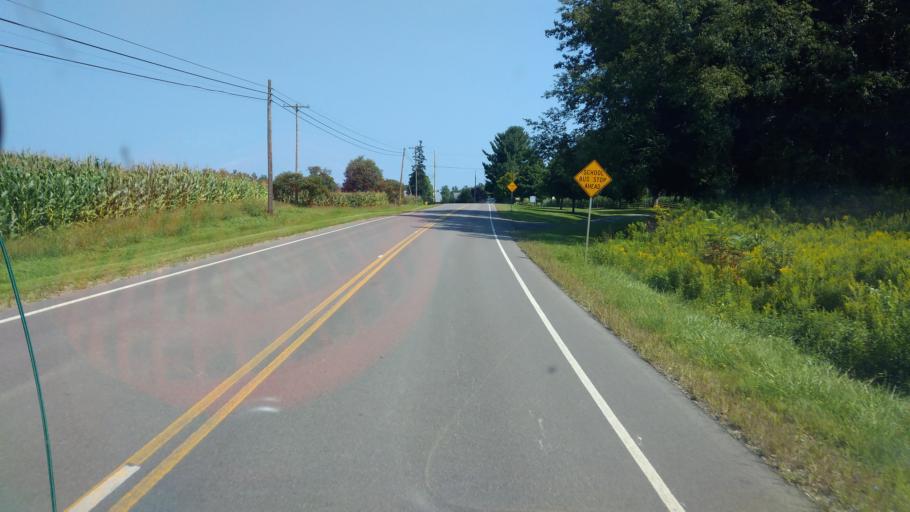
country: US
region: New York
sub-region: Allegany County
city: Belmont
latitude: 42.2659
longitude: -78.0517
